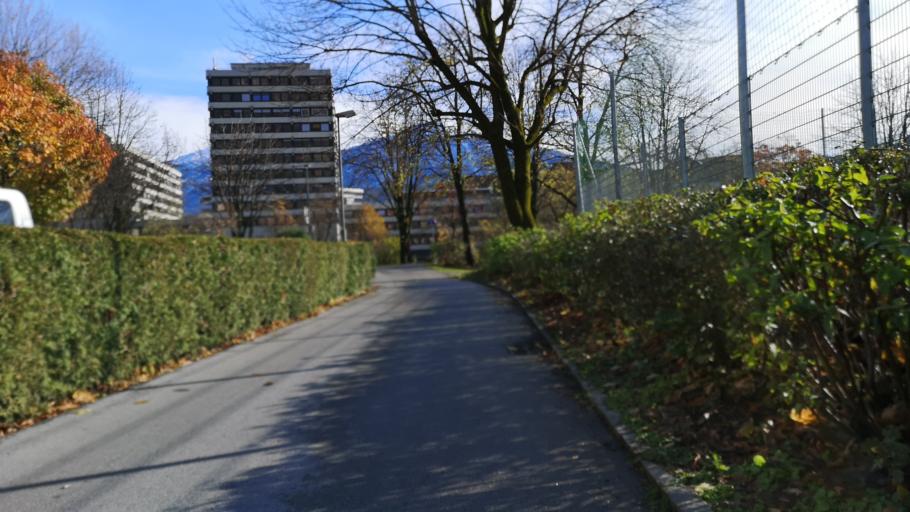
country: AT
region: Tyrol
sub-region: Innsbruck Stadt
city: Innsbruck
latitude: 47.2650
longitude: 11.3825
